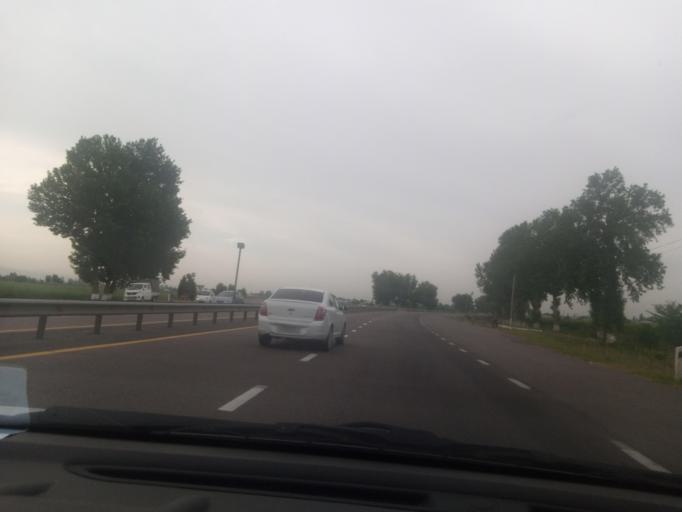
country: UZ
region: Toshkent Shahri
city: Bektemir
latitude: 41.1452
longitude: 69.4311
